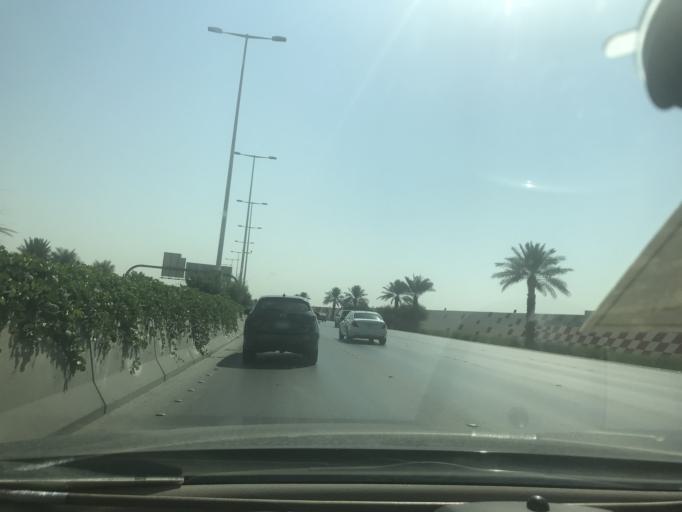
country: SA
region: Ar Riyad
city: Riyadh
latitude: 24.7245
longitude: 46.7104
